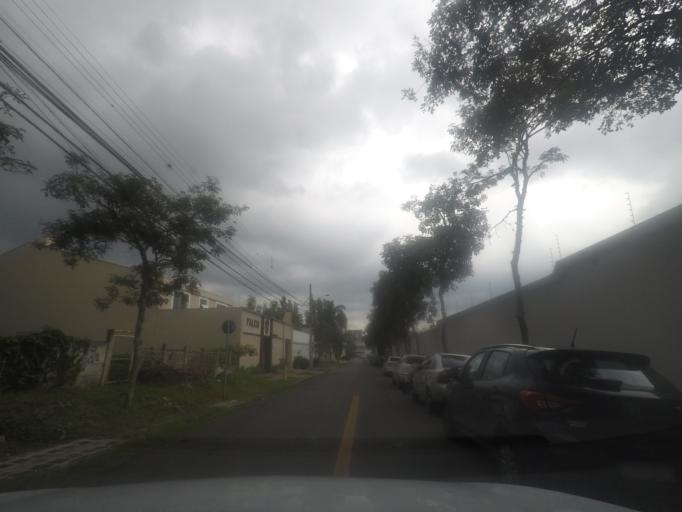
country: BR
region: Parana
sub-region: Curitiba
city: Curitiba
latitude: -25.4503
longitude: -49.3063
